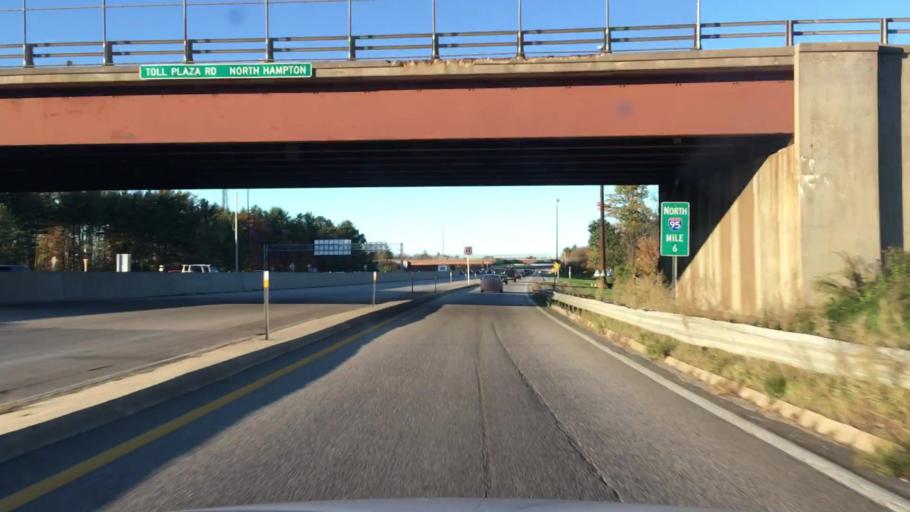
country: US
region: New Hampshire
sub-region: Rockingham County
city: North Hampton
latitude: 42.9651
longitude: -70.8553
